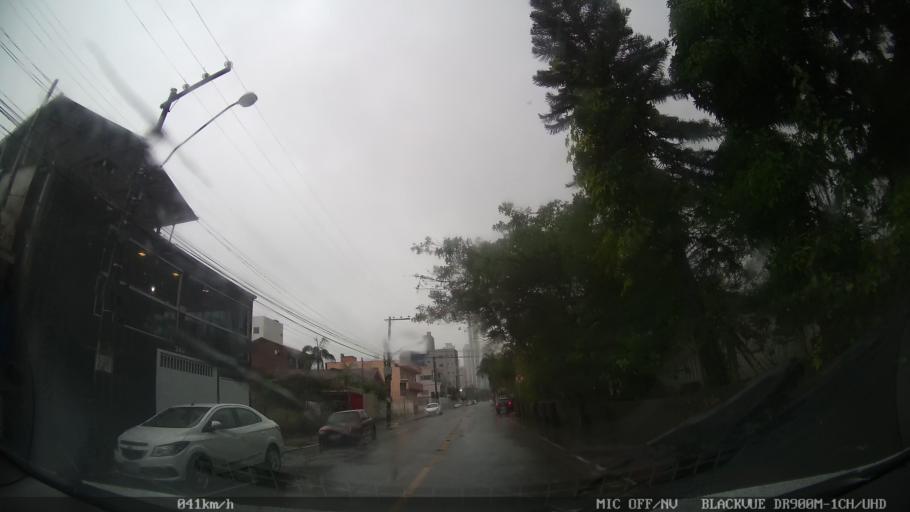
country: BR
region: Santa Catarina
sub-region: Balneario Camboriu
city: Balneario Camboriu
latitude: -27.0089
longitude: -48.6261
